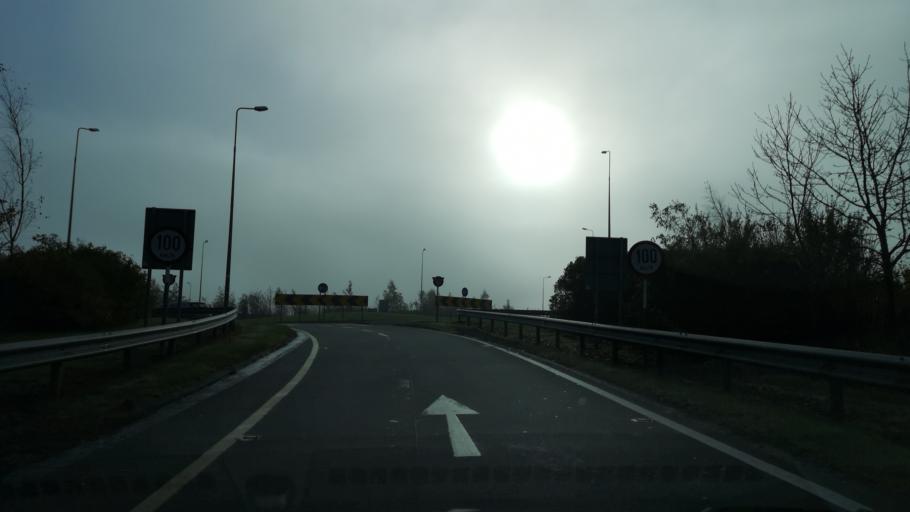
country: IE
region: Leinster
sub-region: An Iarmhi
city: Athlone
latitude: 53.4160
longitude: -7.8883
